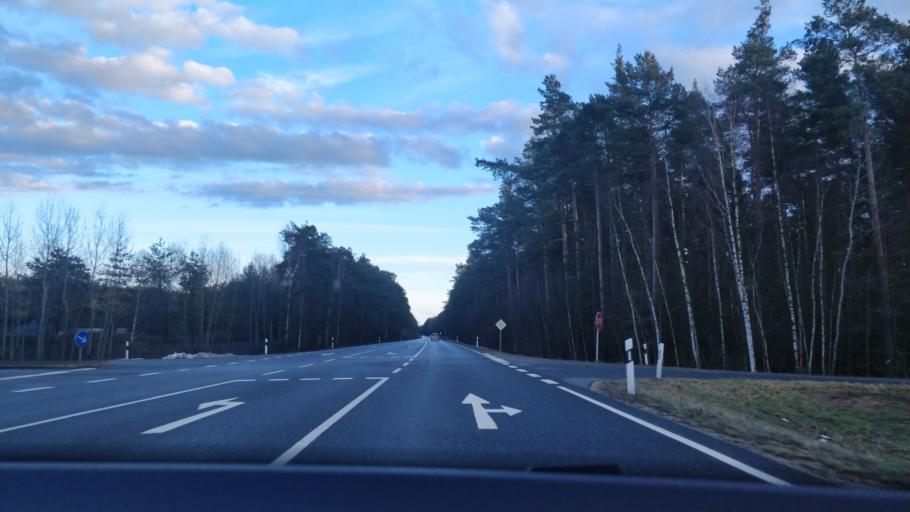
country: DE
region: Bavaria
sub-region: Upper Palatinate
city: Pressath
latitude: 49.7383
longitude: 11.9500
